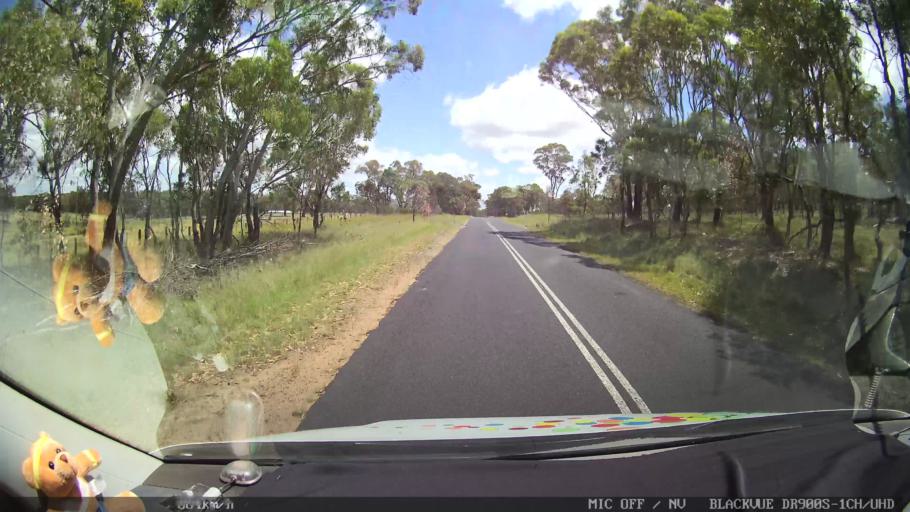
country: AU
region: New South Wales
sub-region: Glen Innes Severn
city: Glen Innes
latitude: -29.5283
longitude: 151.6736
